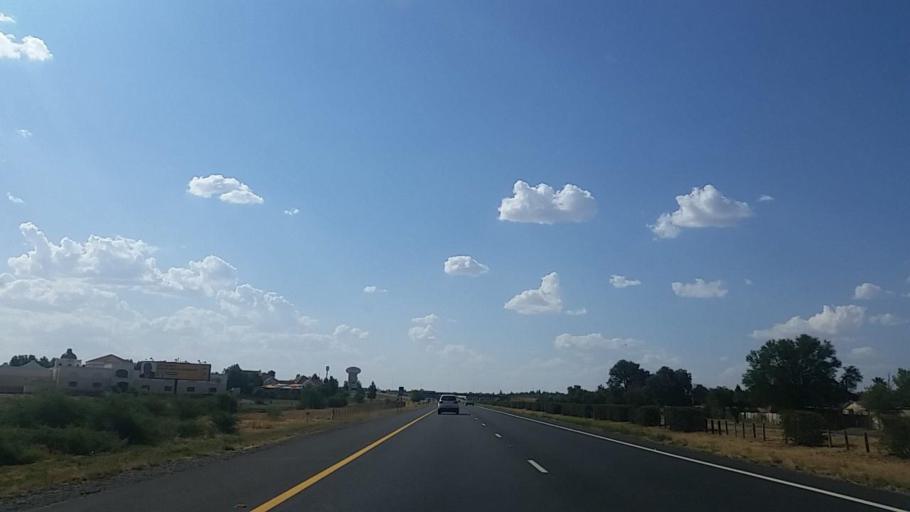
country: ZA
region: Orange Free State
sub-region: Mangaung Metropolitan Municipality
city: Bloemfontein
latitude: -29.1712
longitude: 26.1846
